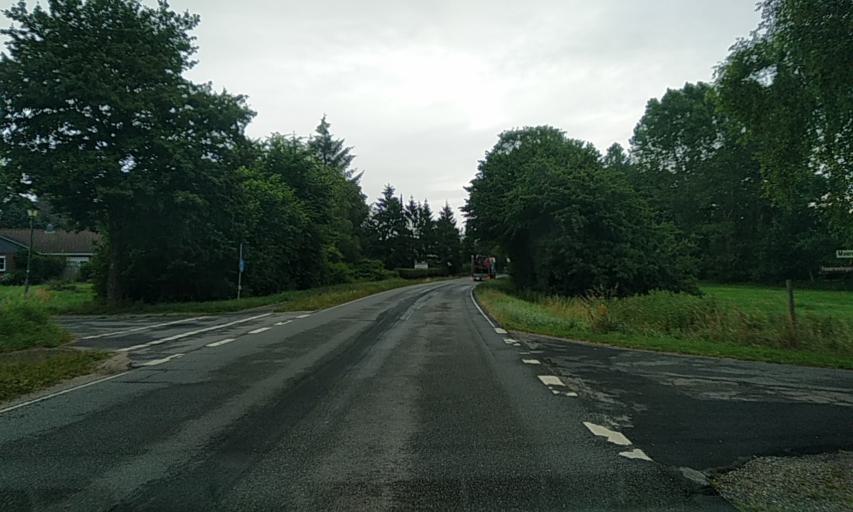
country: DE
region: Schleswig-Holstein
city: Boel
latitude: 54.6455
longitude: 9.7206
